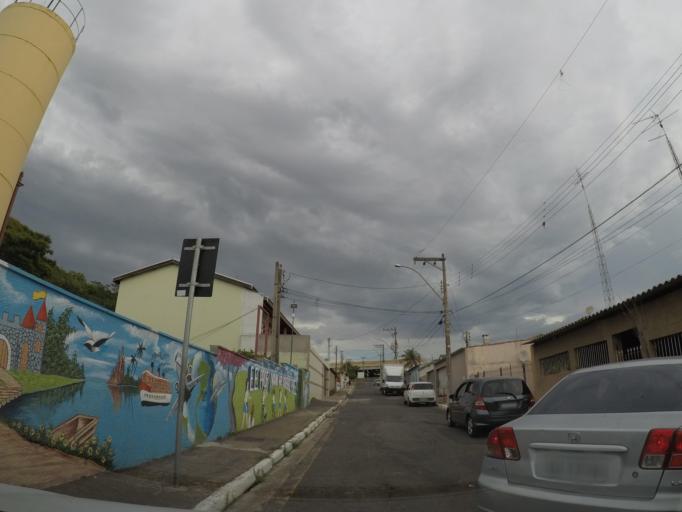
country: BR
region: Sao Paulo
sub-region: Sumare
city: Sumare
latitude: -22.8179
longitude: -47.2542
